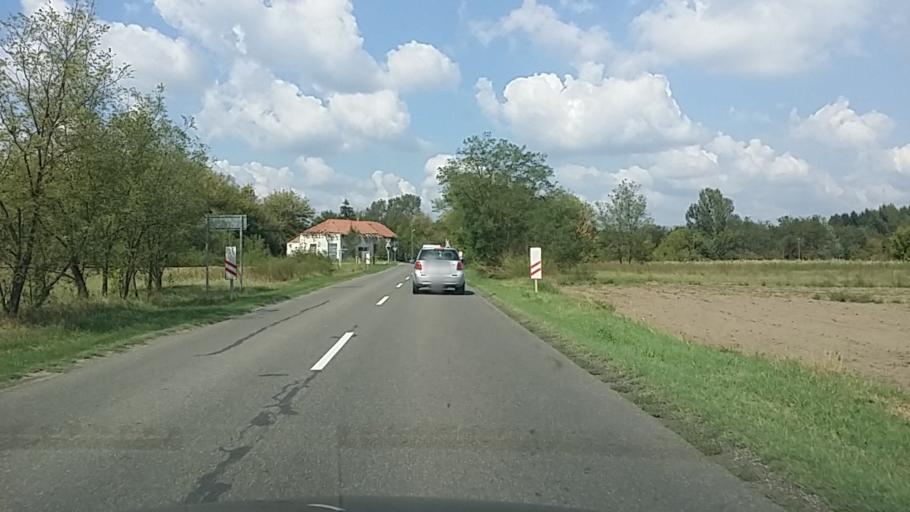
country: HU
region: Bacs-Kiskun
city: Tiszaalpar
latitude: 46.8327
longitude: 19.9738
